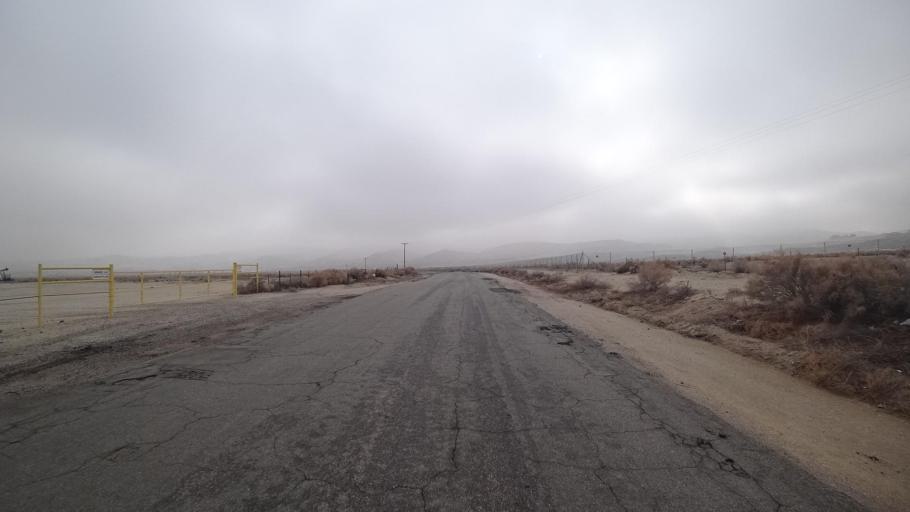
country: US
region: California
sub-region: Kern County
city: Maricopa
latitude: 35.0517
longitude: -119.3934
